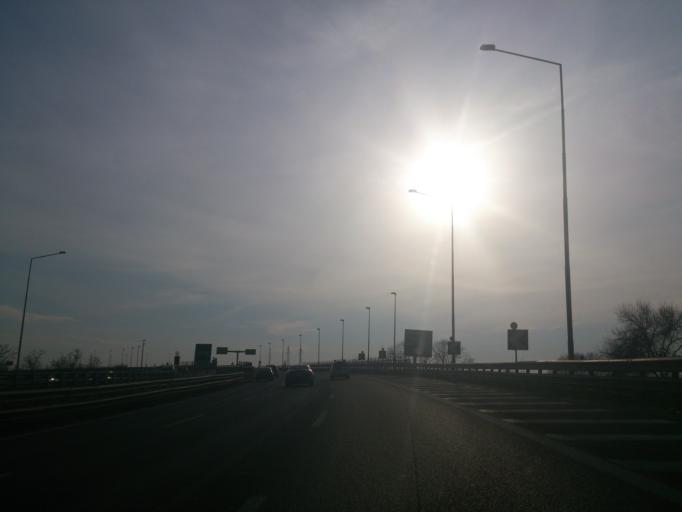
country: IT
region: Lombardy
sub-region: Citta metropolitana di Milano
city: Chiaravalle
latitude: 45.4282
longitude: 9.2468
